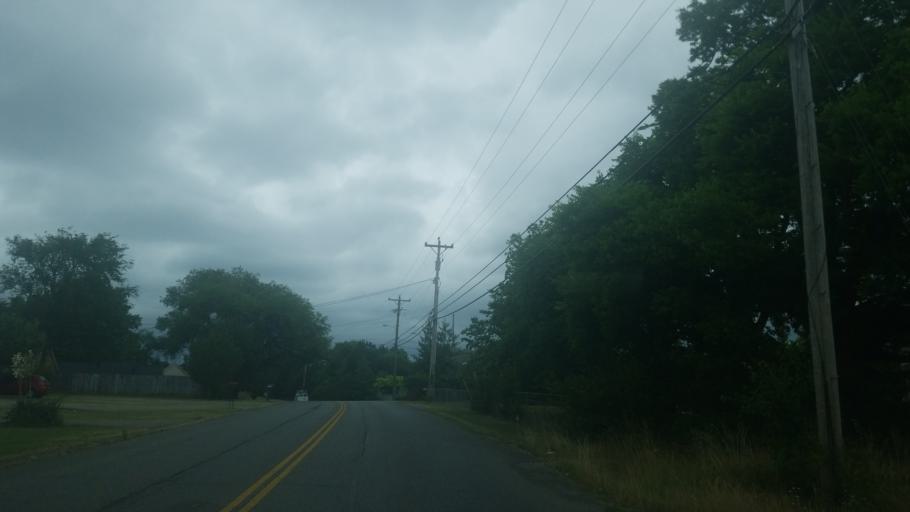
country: US
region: Tennessee
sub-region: Rutherford County
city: La Vergne
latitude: 36.0325
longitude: -86.5876
